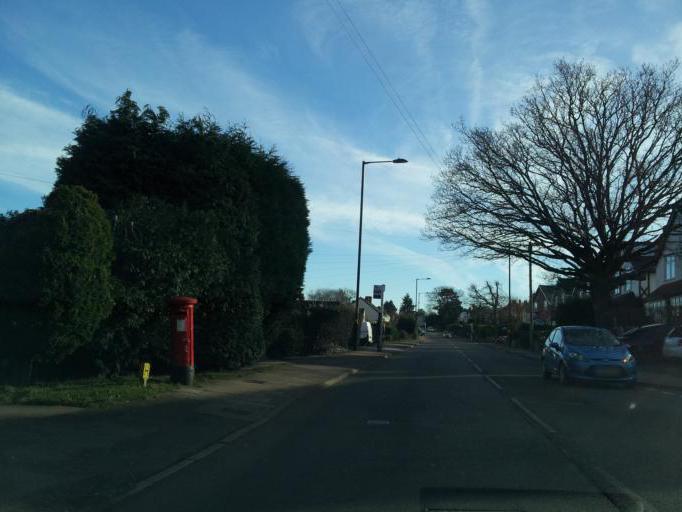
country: GB
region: England
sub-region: City and Borough of Birmingham
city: Sutton Coldfield
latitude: 52.5924
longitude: -1.8423
